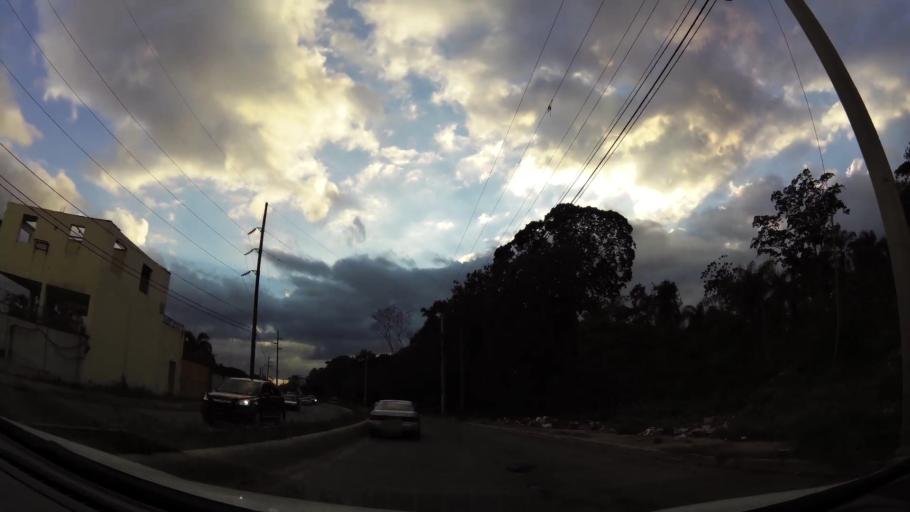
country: DO
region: Santo Domingo
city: Santo Domingo Oeste
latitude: 18.5078
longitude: -69.9968
